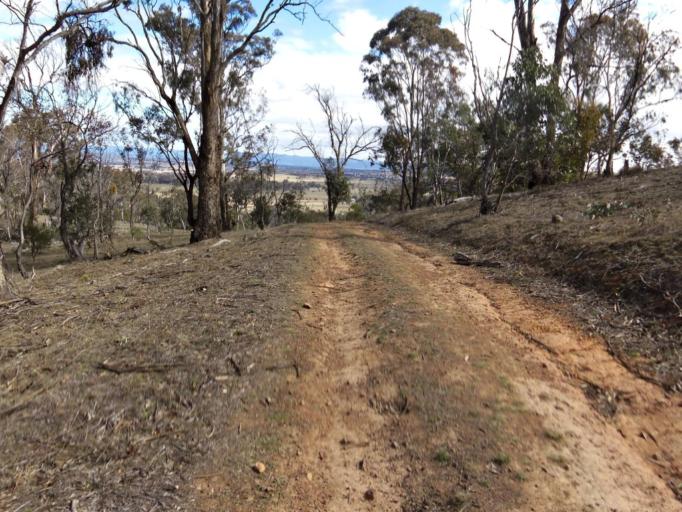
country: AU
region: Australian Capital Territory
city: Kaleen
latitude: -35.2104
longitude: 149.1850
